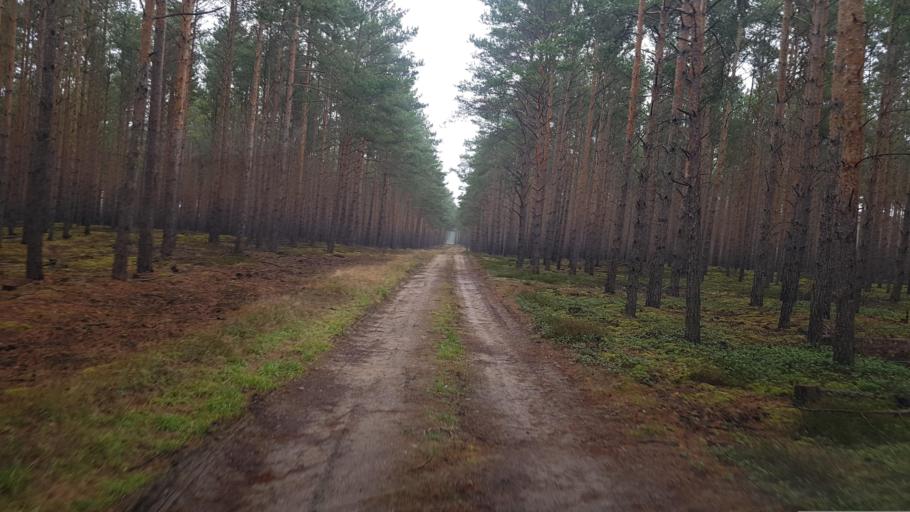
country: DE
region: Brandenburg
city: Sallgast
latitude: 51.6461
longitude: 13.8153
